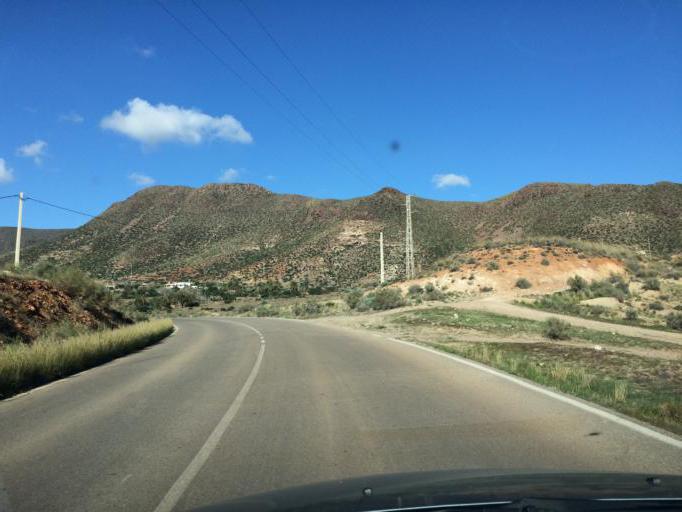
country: ES
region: Andalusia
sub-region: Provincia de Almeria
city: San Jose
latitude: 36.8173
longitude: -2.0532
